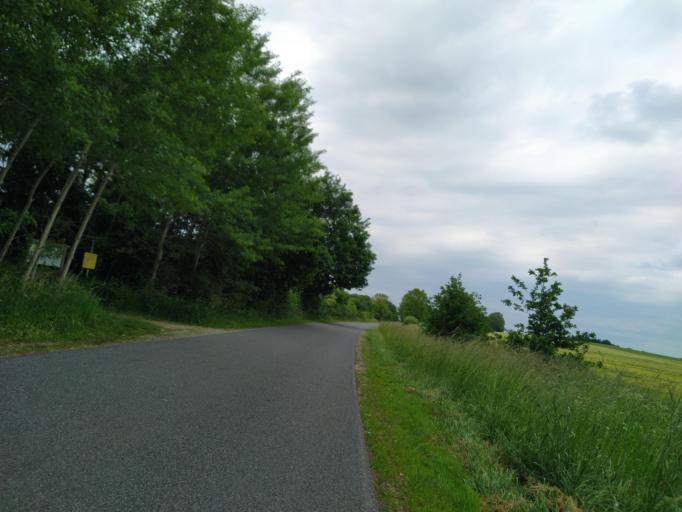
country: DE
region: Schleswig-Holstein
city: Gross Gronau
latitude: 53.7950
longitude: 10.7269
